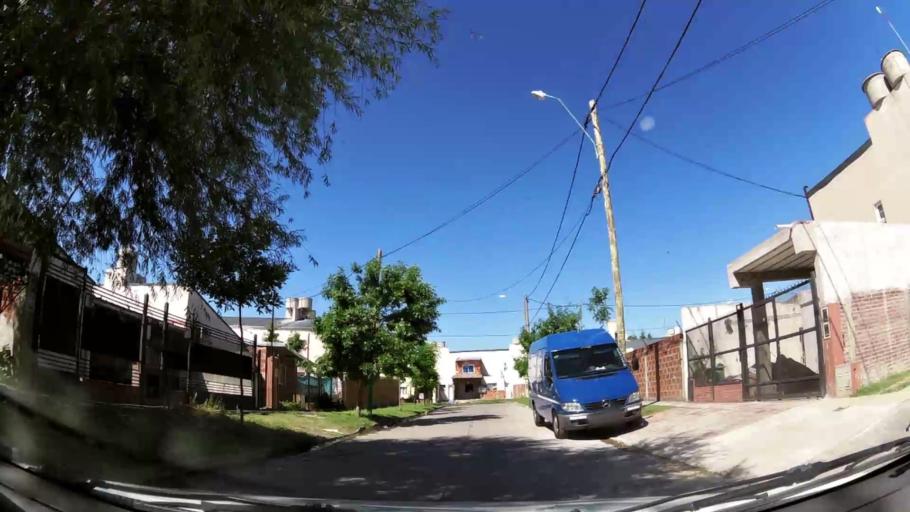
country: AR
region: Buenos Aires
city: Hurlingham
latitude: -34.6198
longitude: -58.6518
